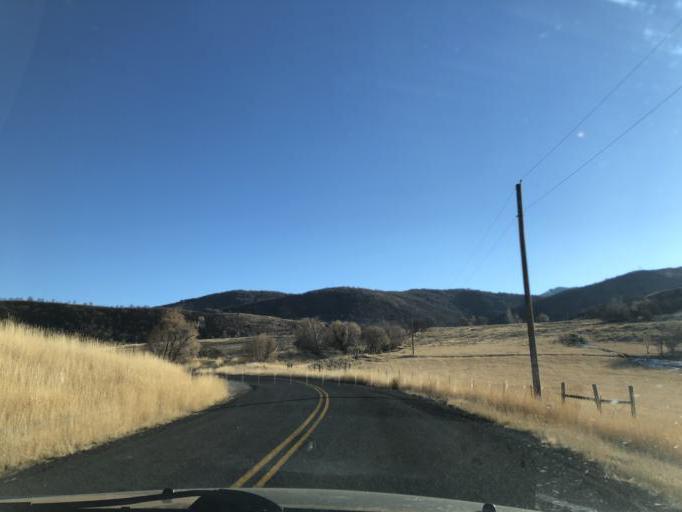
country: US
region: Utah
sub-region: Cache County
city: Wellsville
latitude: 41.5820
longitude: -111.9253
